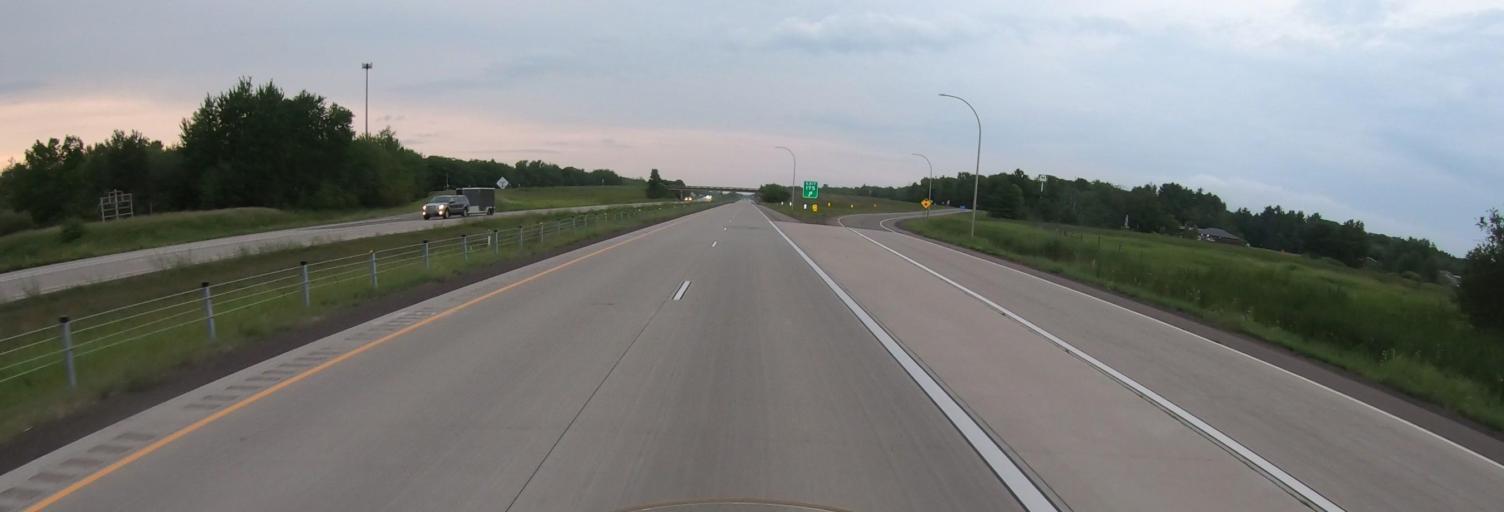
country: US
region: Minnesota
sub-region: Pine County
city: Pine City
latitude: 45.9010
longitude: -92.9666
